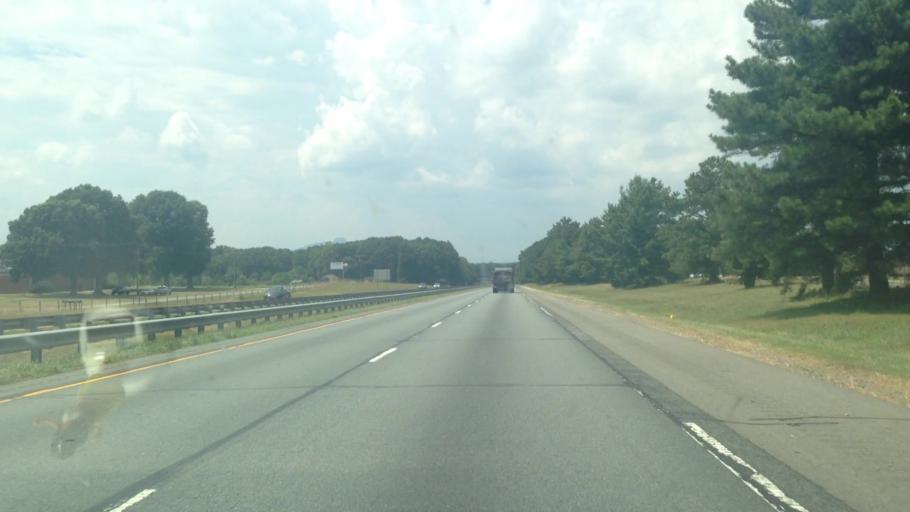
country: US
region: North Carolina
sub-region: Stokes County
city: King
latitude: 36.2661
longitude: -80.3705
